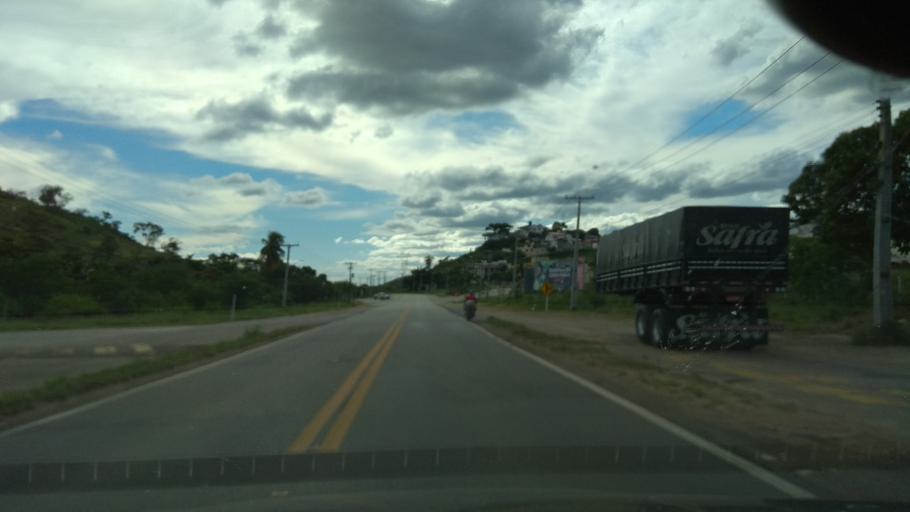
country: BR
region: Bahia
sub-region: Jequie
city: Jequie
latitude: -13.8748
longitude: -40.0401
